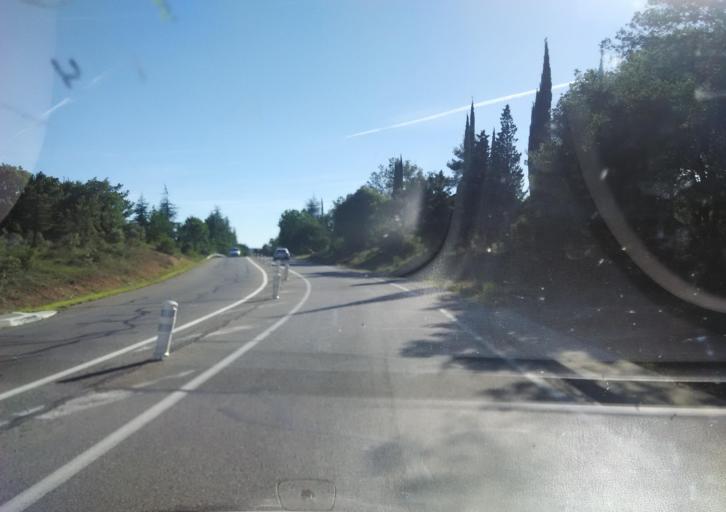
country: FR
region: Provence-Alpes-Cote d'Azur
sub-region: Departement du Var
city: Vinon-sur-Verdon
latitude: 43.7122
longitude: 5.7738
